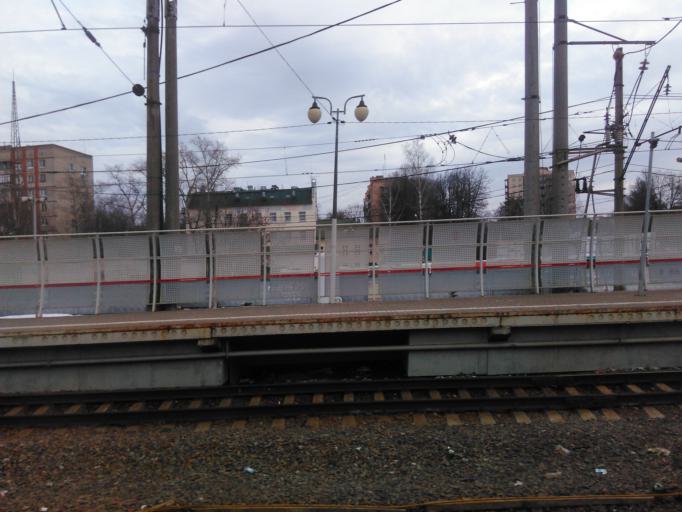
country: RU
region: Moskovskaya
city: Pushkino
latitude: 56.0101
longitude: 37.8383
